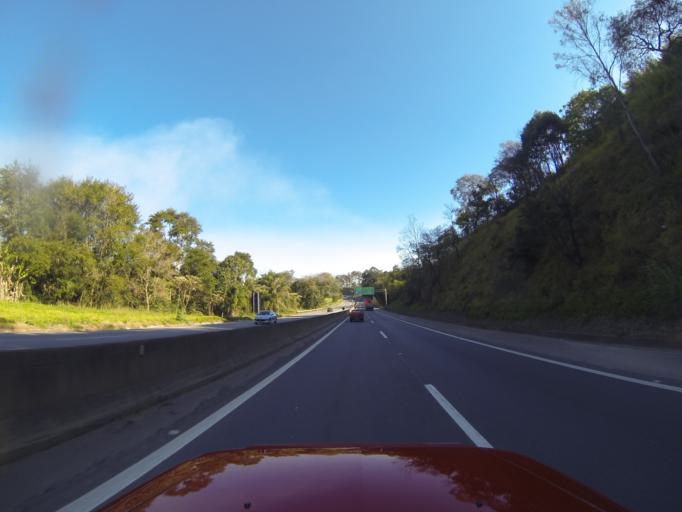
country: BR
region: Sao Paulo
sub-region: Atibaia
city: Atibaia
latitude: -23.0891
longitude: -46.5720
